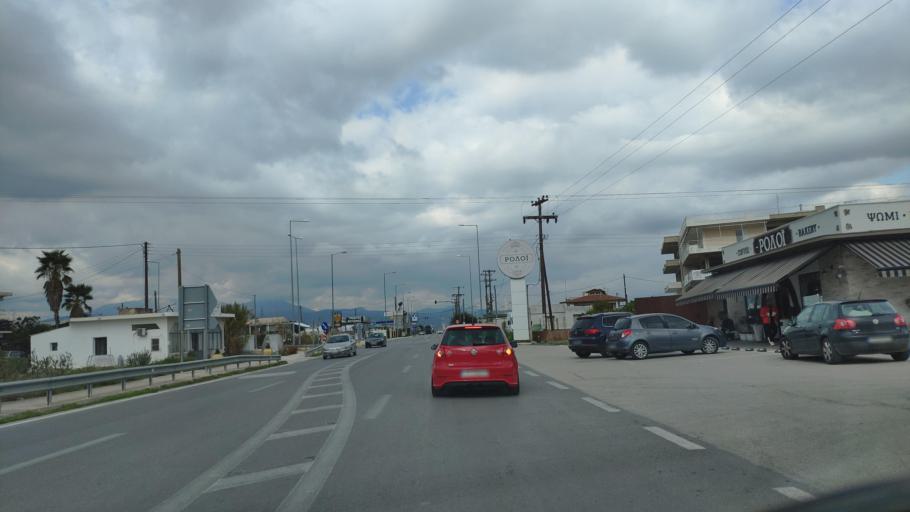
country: GR
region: Peloponnese
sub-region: Nomos Argolidos
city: Argos
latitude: 37.6494
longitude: 22.7291
